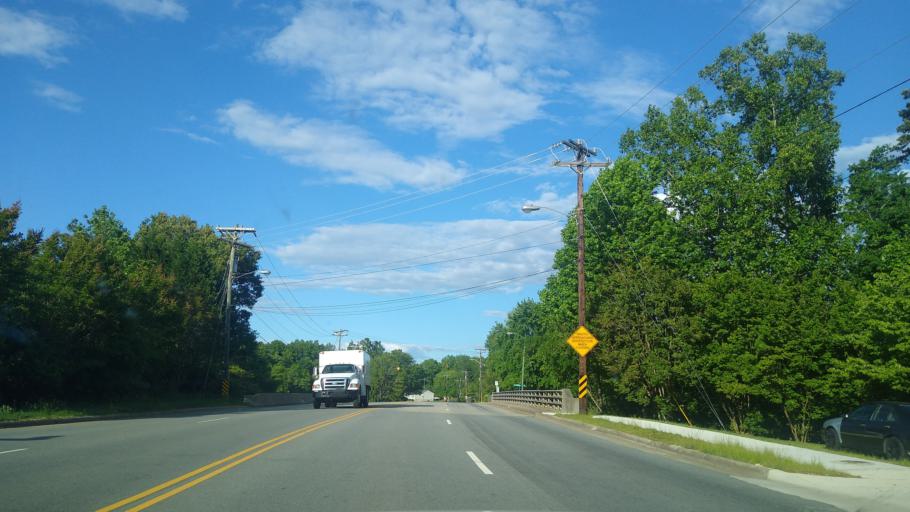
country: US
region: North Carolina
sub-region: Guilford County
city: Greensboro
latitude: 36.1453
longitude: -79.7584
